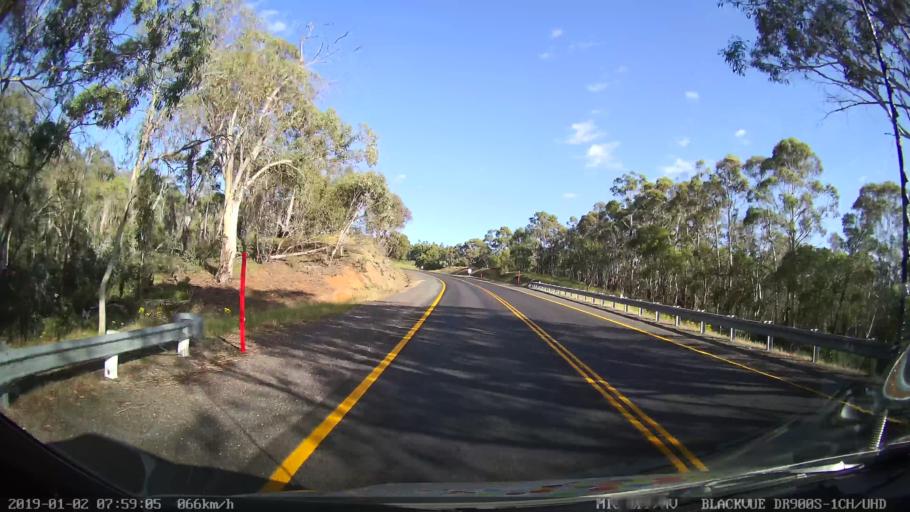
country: AU
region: New South Wales
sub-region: Tumut Shire
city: Tumut
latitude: -35.6474
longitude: 148.4617
